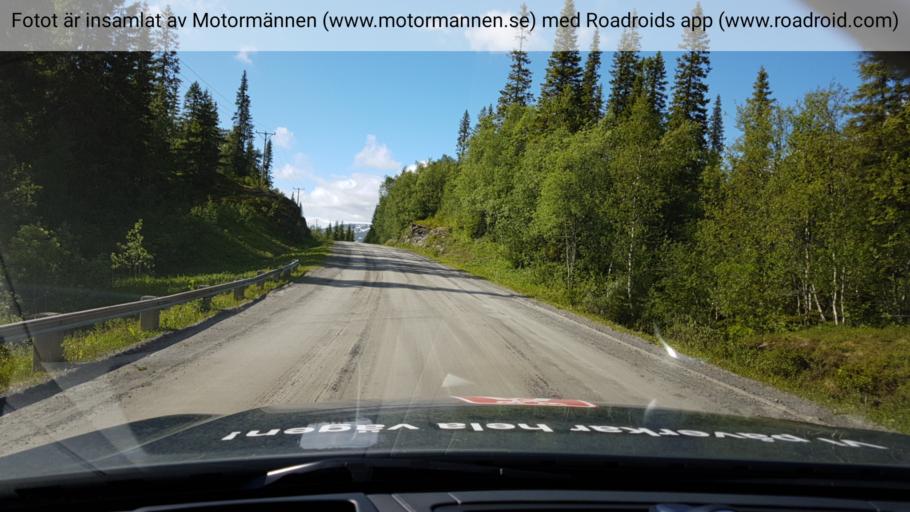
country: SE
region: Jaemtland
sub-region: Are Kommun
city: Are
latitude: 63.6773
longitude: 12.8167
